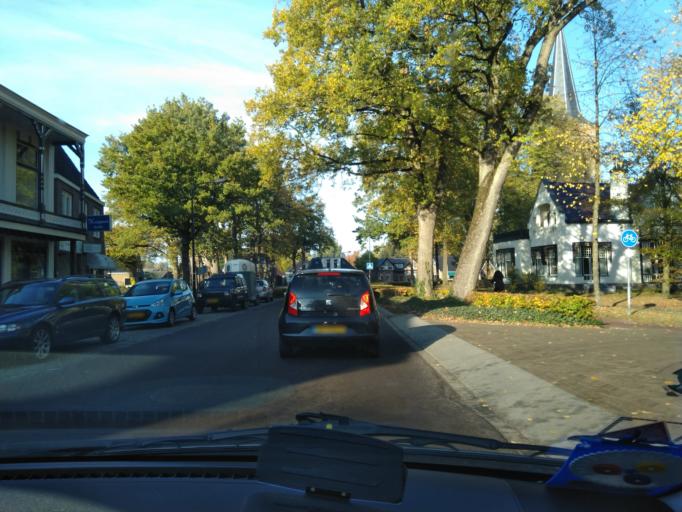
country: NL
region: Drenthe
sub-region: Gemeente Tynaarlo
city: Zuidlaren
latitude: 53.0954
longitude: 6.6870
